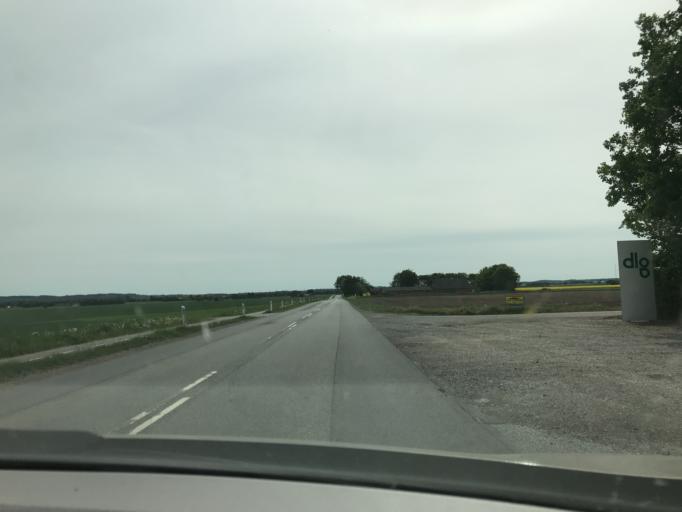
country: DK
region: Central Jutland
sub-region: Norddjurs Kommune
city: Allingabro
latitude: 56.4925
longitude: 10.3281
